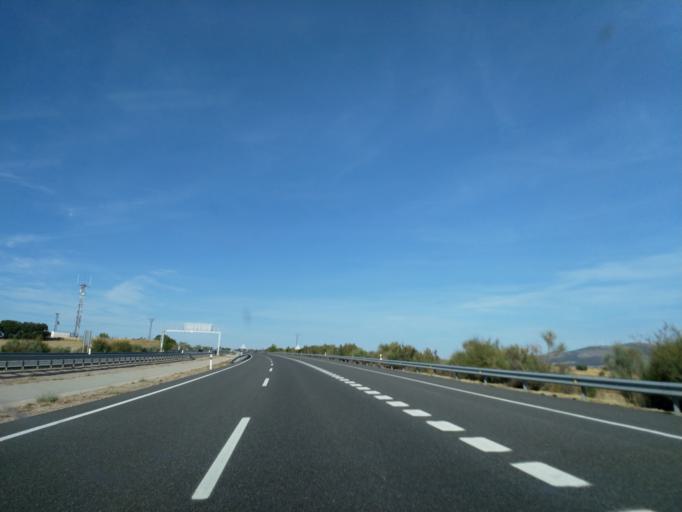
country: ES
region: Castille and Leon
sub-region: Provincia de Avila
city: Berrocalejo de Aragona
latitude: 40.6925
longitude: -4.5853
